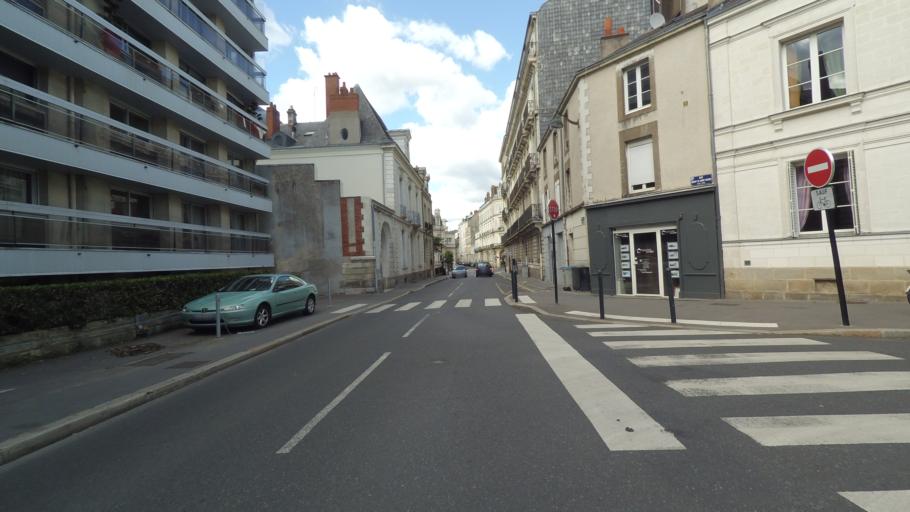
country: FR
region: Pays de la Loire
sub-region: Departement de la Loire-Atlantique
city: Nantes
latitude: 47.2139
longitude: -1.5674
